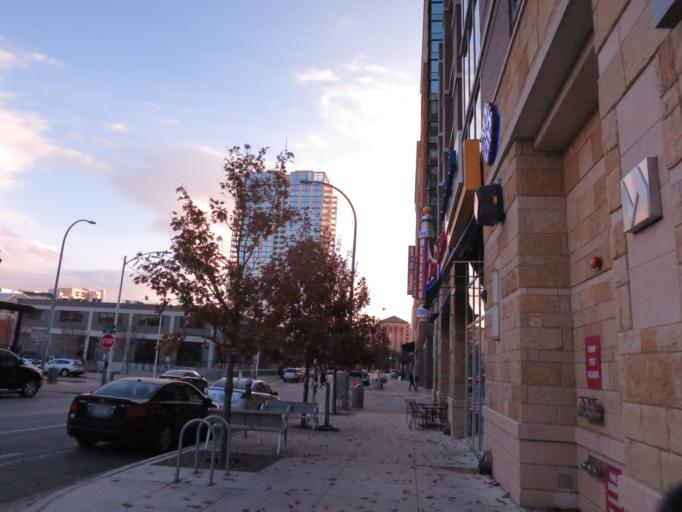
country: US
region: Texas
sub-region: Travis County
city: Austin
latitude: 30.2651
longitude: -97.7414
